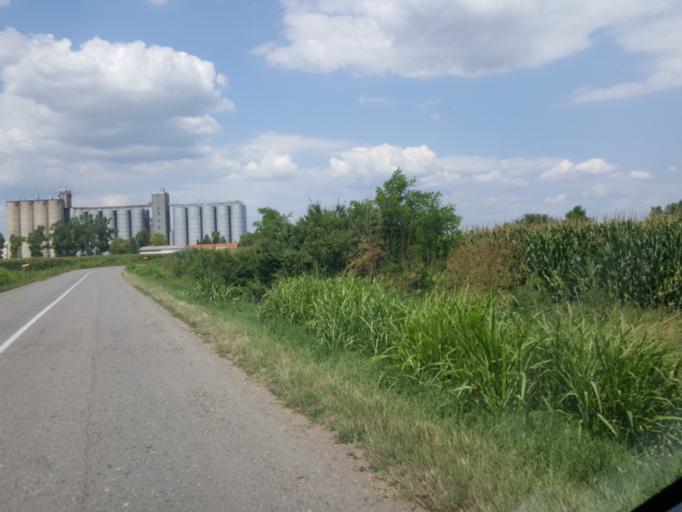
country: RS
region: Autonomna Pokrajina Vojvodina
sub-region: Sremski Okrug
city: Pecinci
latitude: 44.8812
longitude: 19.9606
